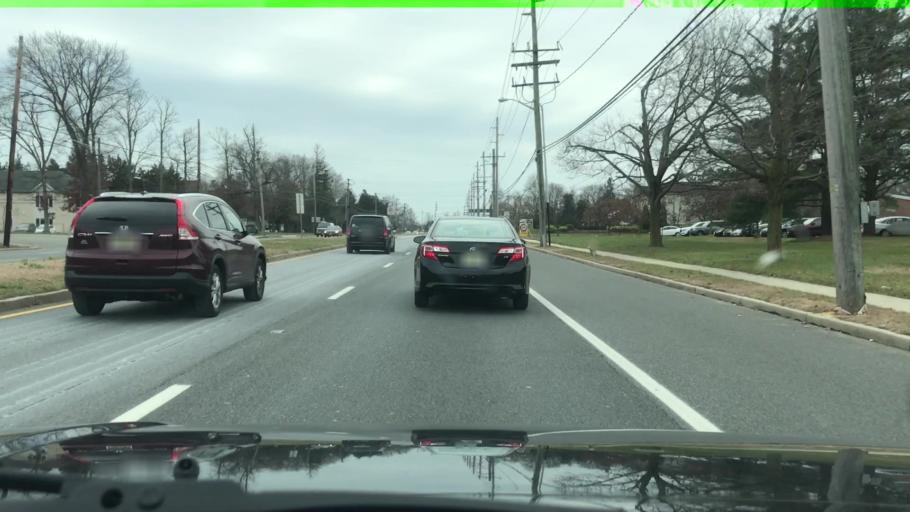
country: US
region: New Jersey
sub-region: Ocean County
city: Toms River
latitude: 39.9715
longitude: -74.1840
